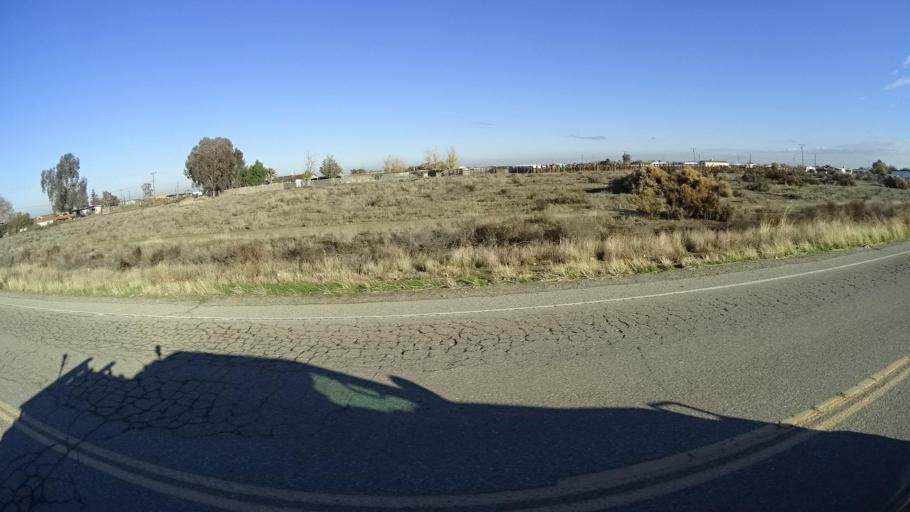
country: US
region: California
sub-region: Kern County
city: Delano
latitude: 35.7757
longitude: -119.3357
